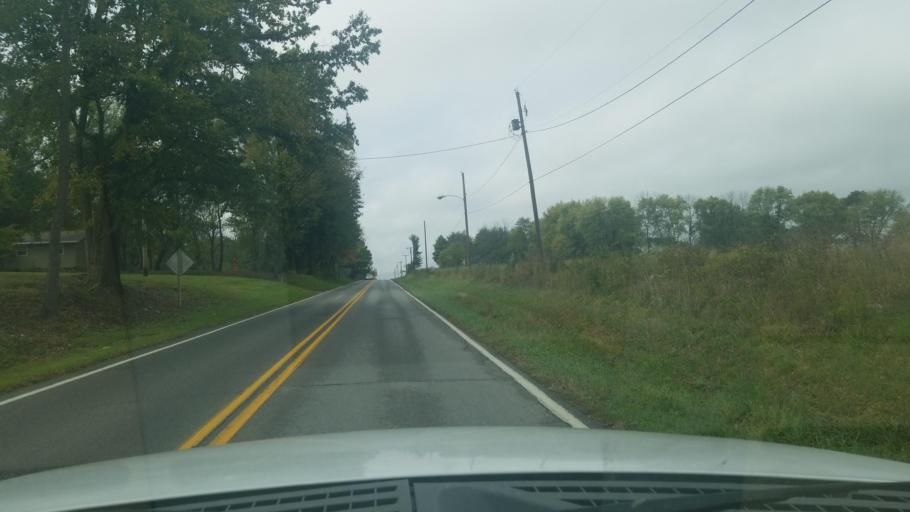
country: US
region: Illinois
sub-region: Saline County
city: Harrisburg
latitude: 37.8414
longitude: -88.6209
